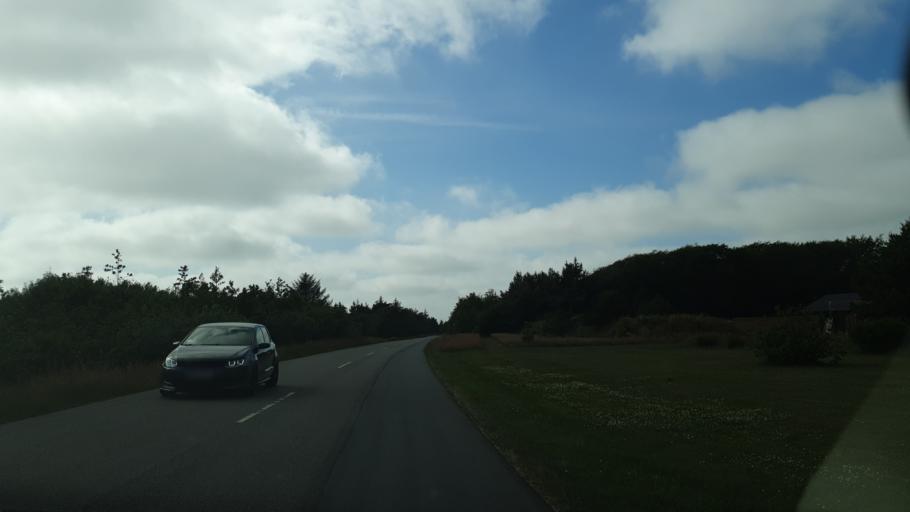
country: DK
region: Central Jutland
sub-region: Ringkobing-Skjern Kommune
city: Ringkobing
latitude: 56.1403
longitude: 8.1508
